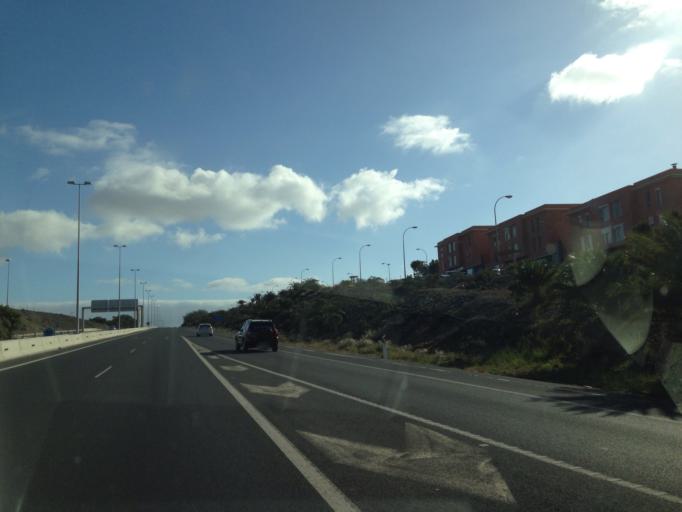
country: ES
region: Canary Islands
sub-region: Provincia de Las Palmas
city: Maspalomas
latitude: 27.7713
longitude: -15.5895
